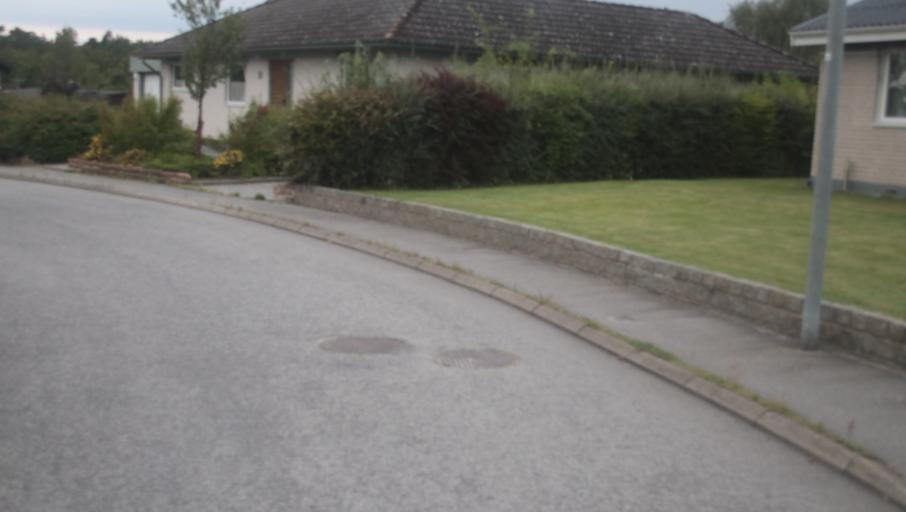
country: SE
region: Blekinge
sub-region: Karlshamns Kommun
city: Karlshamn
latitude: 56.1721
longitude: 14.8853
